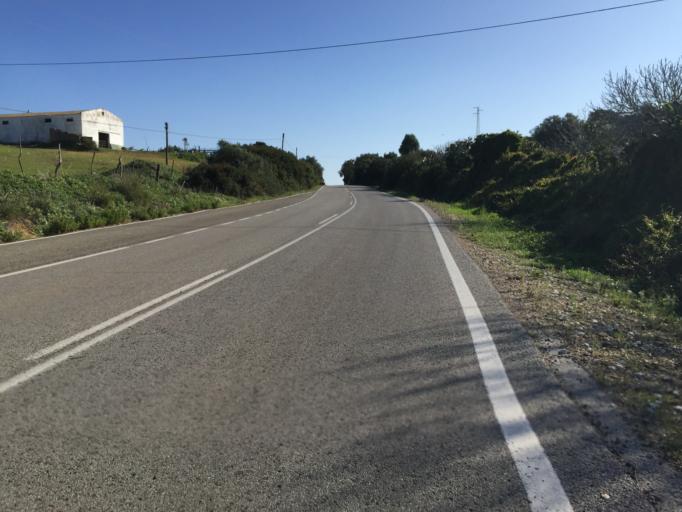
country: ES
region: Andalusia
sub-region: Provincia de Cadiz
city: Vejer de la Frontera
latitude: 36.2691
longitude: -6.0085
